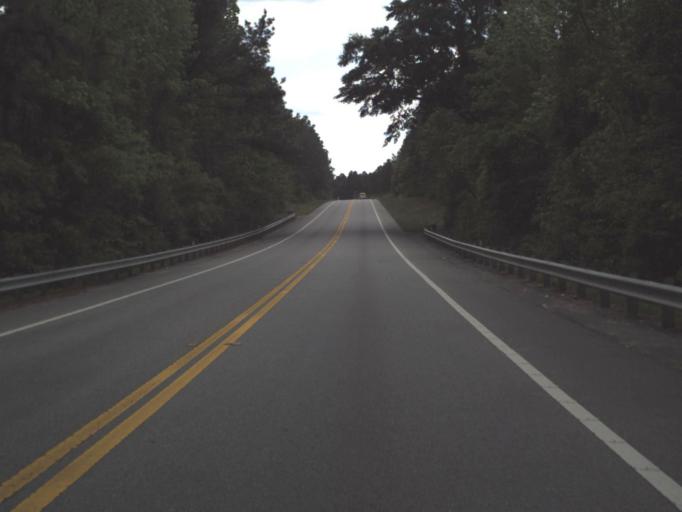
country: US
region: Florida
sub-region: Escambia County
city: Molino
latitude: 30.8264
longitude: -87.4355
